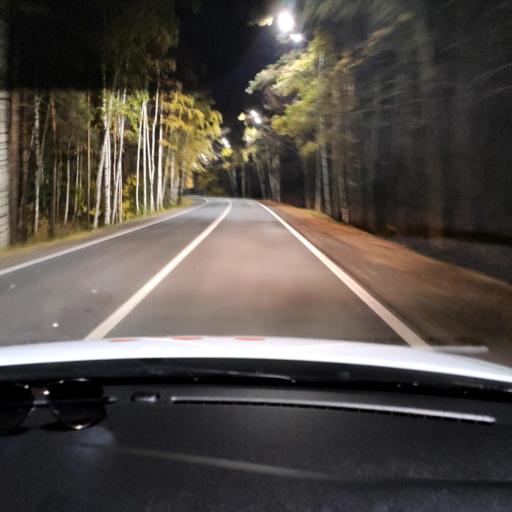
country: RU
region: Tatarstan
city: Verkhniy Uslon
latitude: 55.6325
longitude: 49.0178
